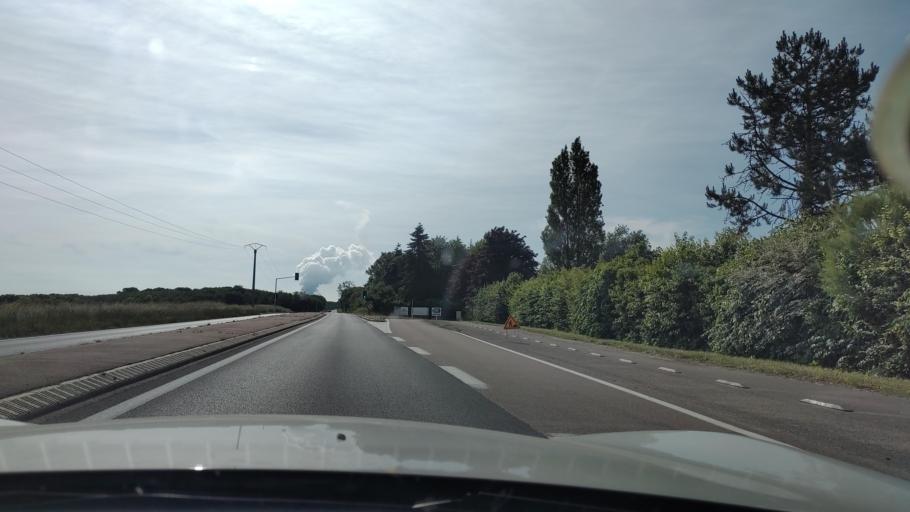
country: FR
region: Ile-de-France
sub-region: Departement de Seine-et-Marne
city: Sourdun
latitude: 48.5339
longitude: 3.3709
